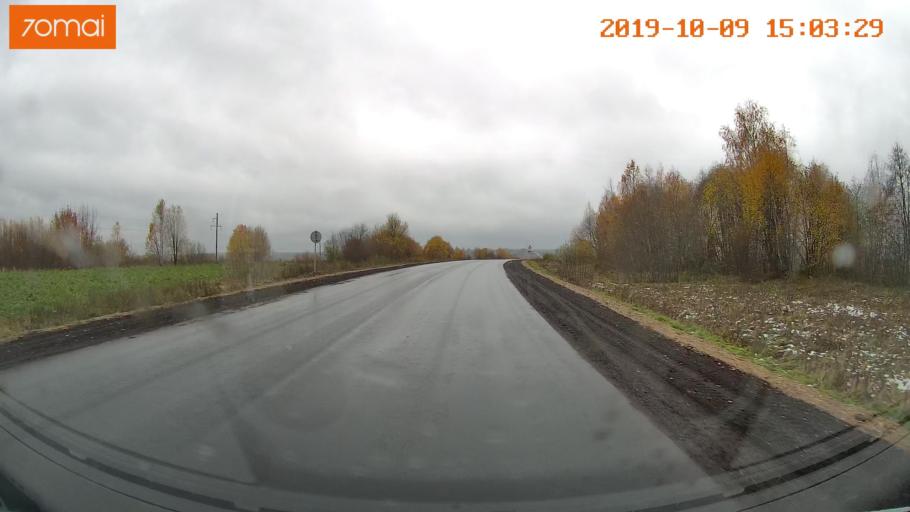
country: RU
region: Kostroma
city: Chistyye Bory
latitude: 58.2707
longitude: 41.6754
